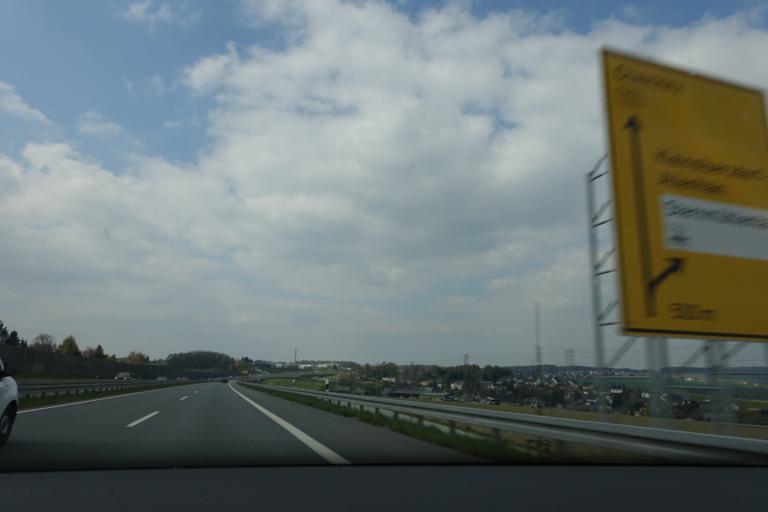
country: DE
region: Saxony
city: Gornau
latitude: 50.7796
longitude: 13.0007
